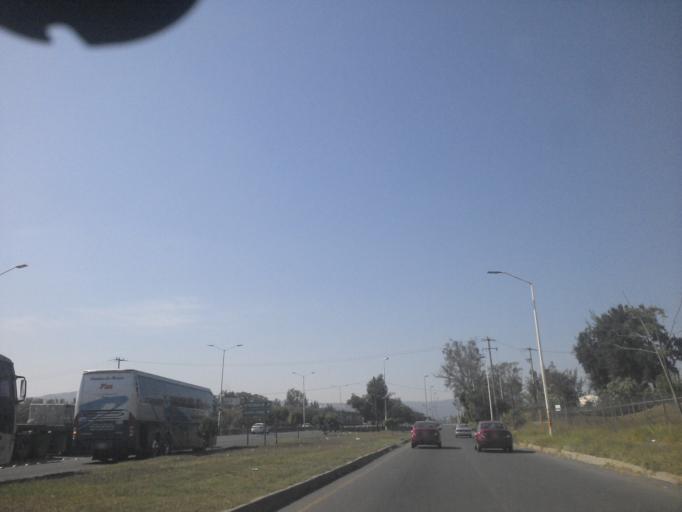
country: MX
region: Jalisco
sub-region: Tlajomulco de Zuniga
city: La Tijera
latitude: 20.6092
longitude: -103.4094
